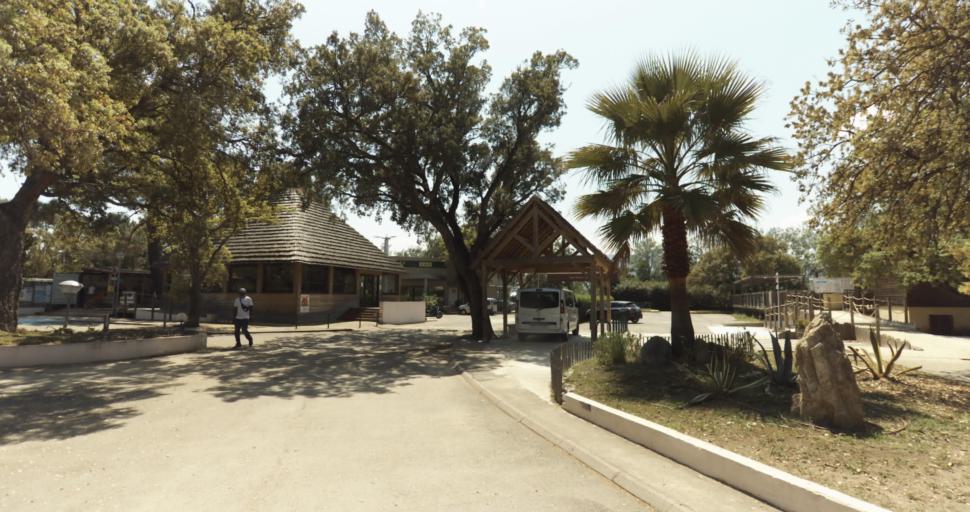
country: FR
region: Corsica
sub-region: Departement de la Haute-Corse
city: Biguglia
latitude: 42.6294
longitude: 9.4677
